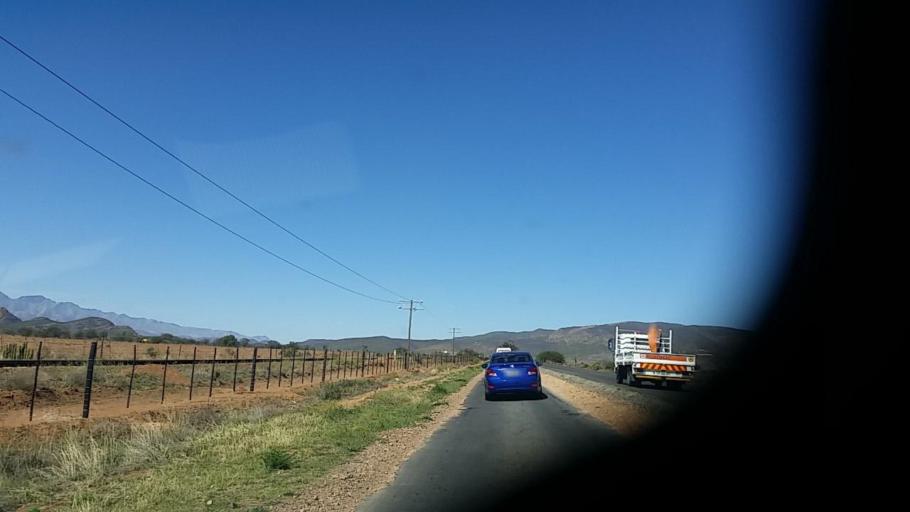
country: ZA
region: Western Cape
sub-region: Eden District Municipality
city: Oudtshoorn
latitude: -33.5612
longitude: 22.4007
